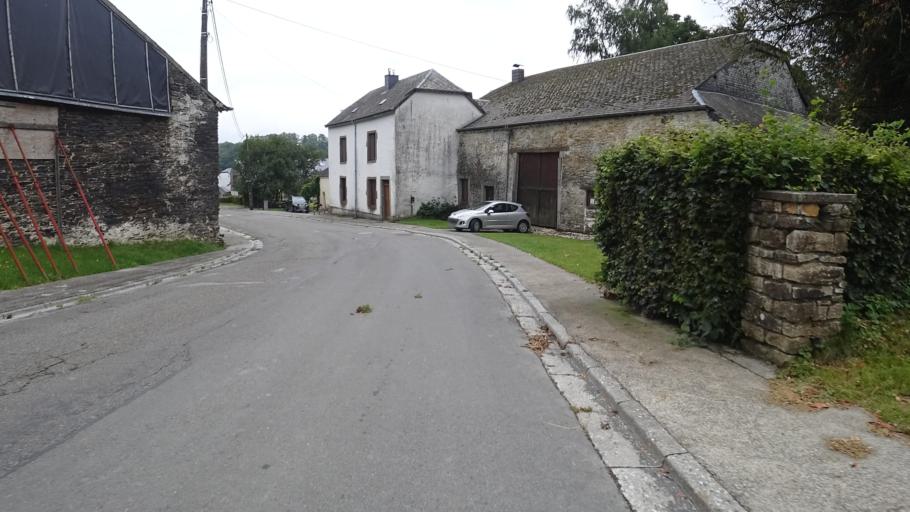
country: BE
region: Wallonia
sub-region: Province du Luxembourg
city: Chiny
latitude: 49.8055
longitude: 5.3584
